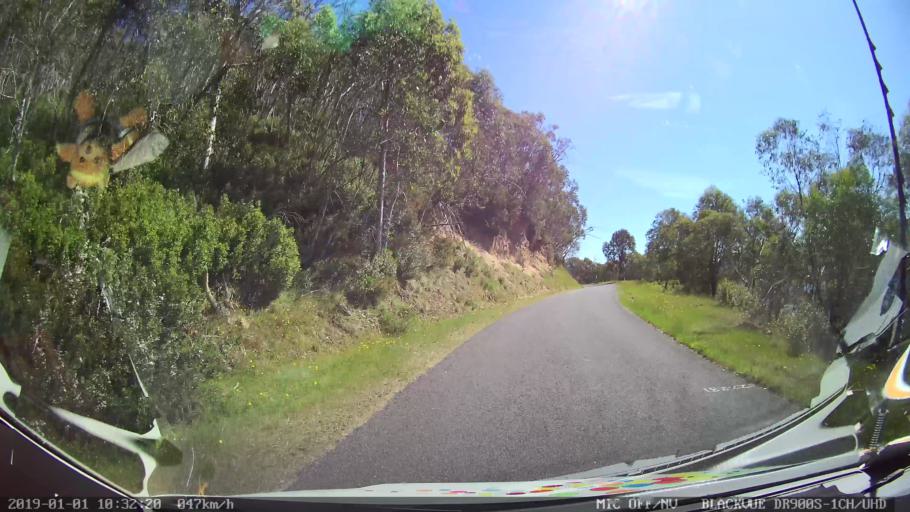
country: AU
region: New South Wales
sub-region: Snowy River
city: Jindabyne
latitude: -36.0545
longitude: 148.2724
